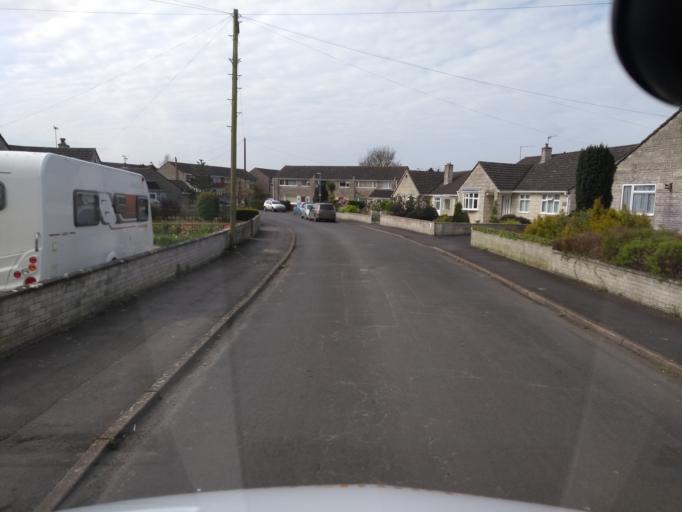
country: GB
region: England
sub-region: Somerset
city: Street
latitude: 51.0514
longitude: -2.7400
